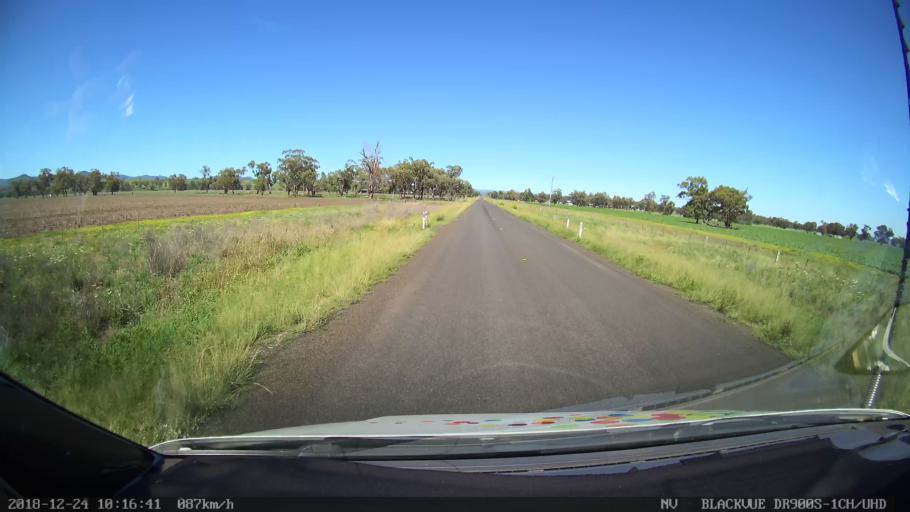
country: AU
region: New South Wales
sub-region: Liverpool Plains
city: Quirindi
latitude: -31.7172
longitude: 150.6024
